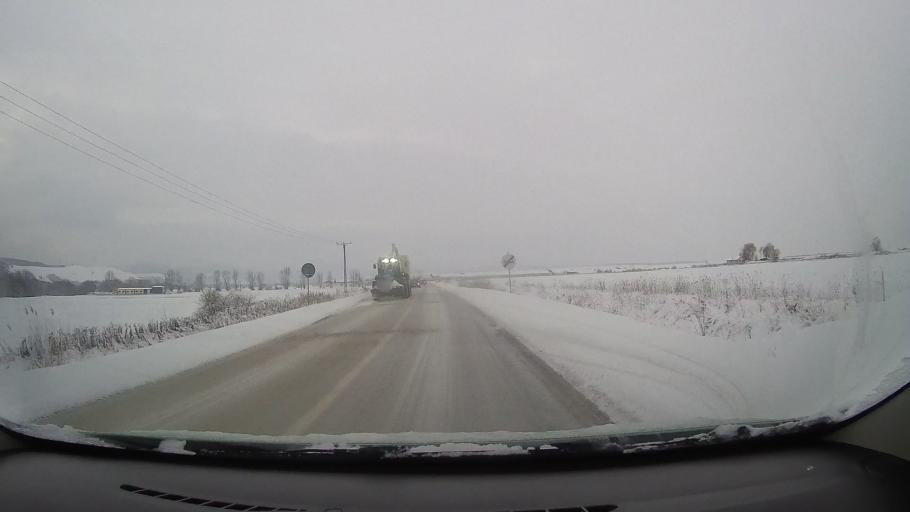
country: RO
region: Alba
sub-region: Comuna Pianu
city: Pianu de Jos
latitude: 45.9646
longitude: 23.4778
